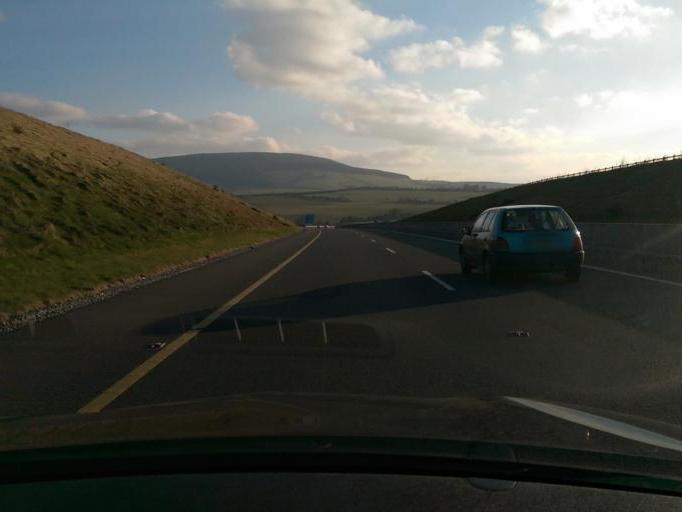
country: IE
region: Munster
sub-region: North Tipperary
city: Roscrea
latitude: 52.8934
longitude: -7.9110
